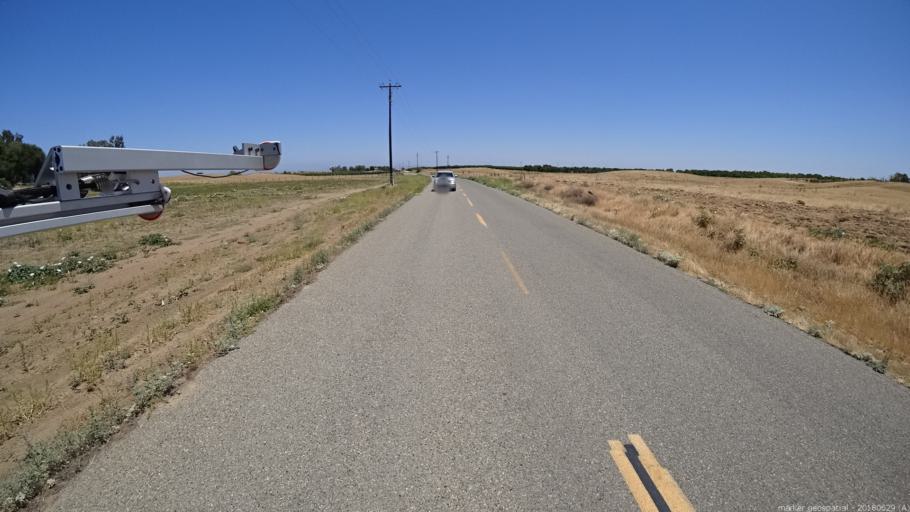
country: US
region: California
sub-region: Madera County
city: Parksdale
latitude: 37.0063
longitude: -119.9767
